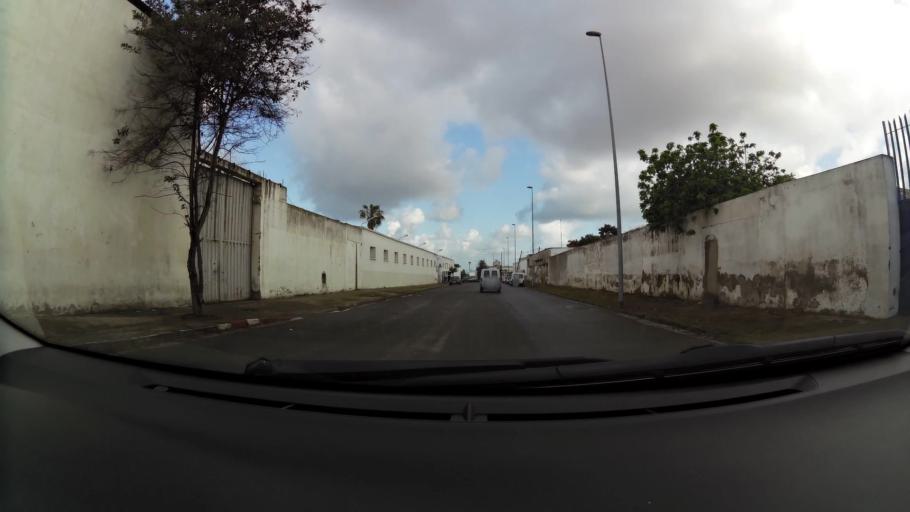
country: MA
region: Grand Casablanca
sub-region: Mediouna
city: Tit Mellil
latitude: 33.5908
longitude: -7.5434
